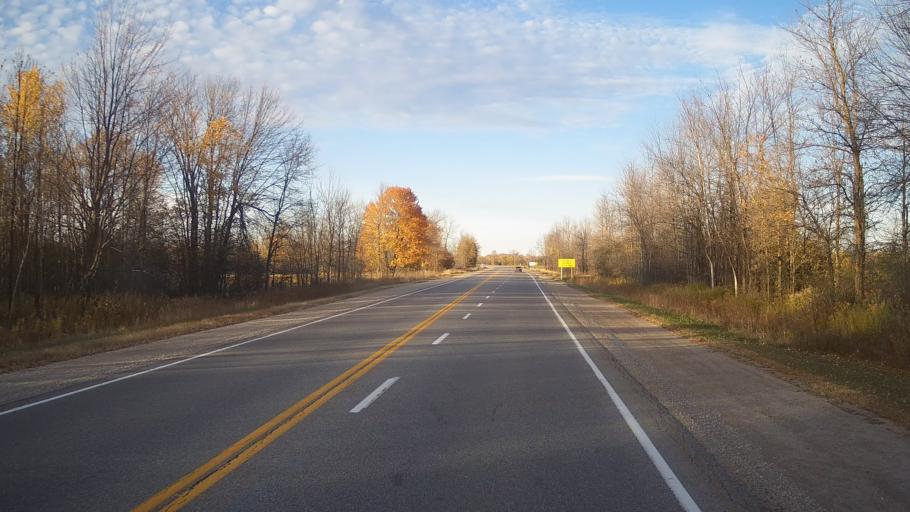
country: CA
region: Ontario
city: Perth
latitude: 44.9719
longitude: -76.2284
